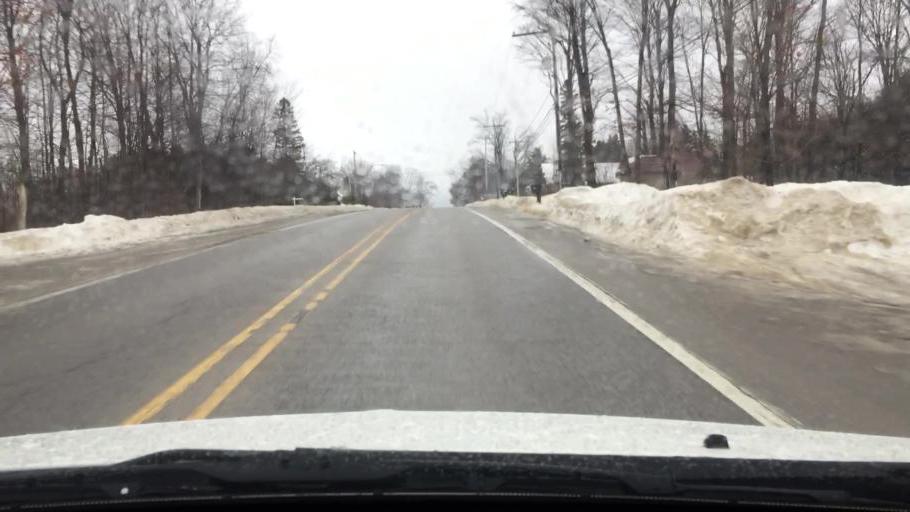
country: US
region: Michigan
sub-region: Charlevoix County
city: East Jordan
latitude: 45.1484
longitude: -85.1399
